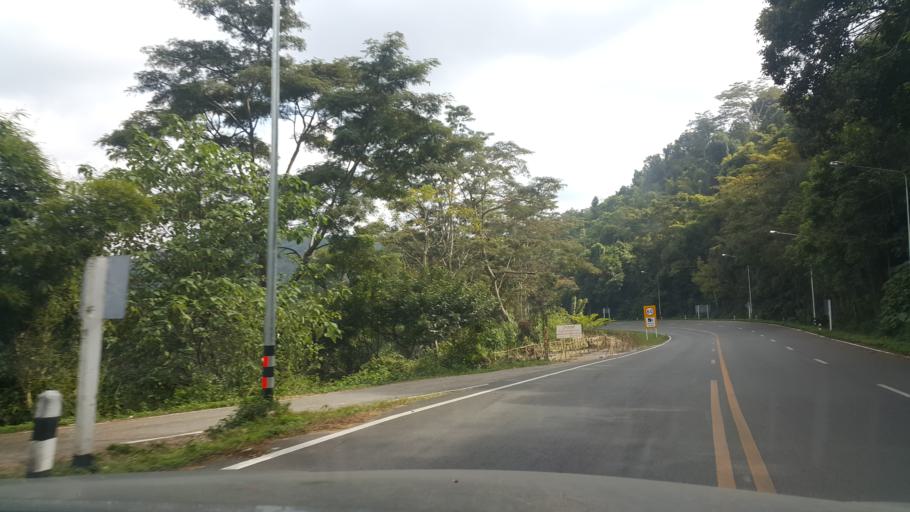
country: TH
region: Phayao
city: Phayao
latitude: 19.0617
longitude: 99.7823
